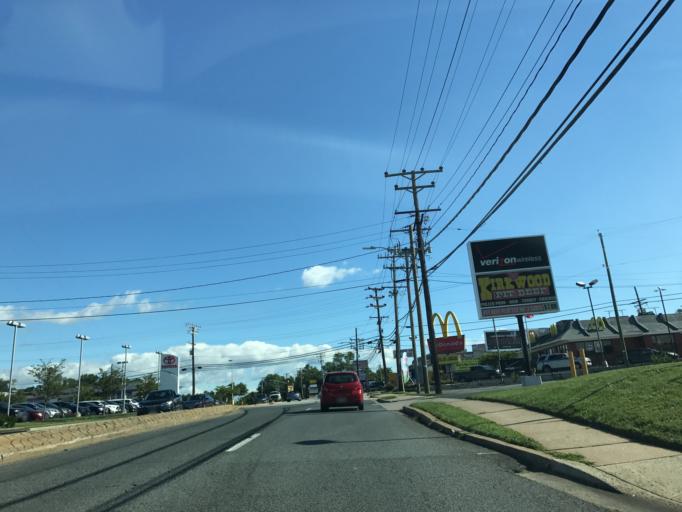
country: US
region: Maryland
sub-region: Baltimore County
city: Catonsville
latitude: 39.2842
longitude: -76.7530
